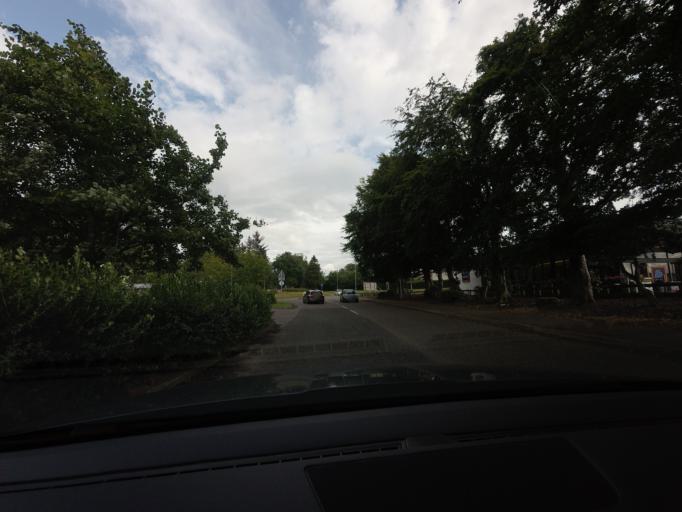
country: GB
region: Scotland
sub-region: Highland
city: Inverness
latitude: 57.4691
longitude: -4.1889
